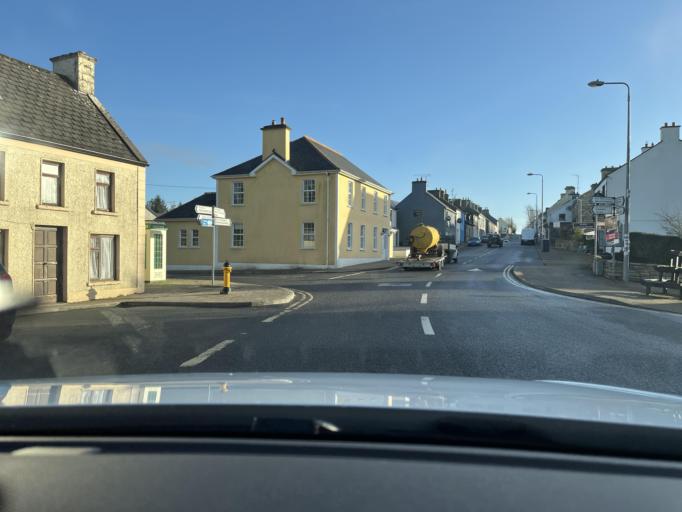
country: IE
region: Connaught
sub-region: County Leitrim
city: Manorhamilton
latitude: 54.1693
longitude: -8.1446
